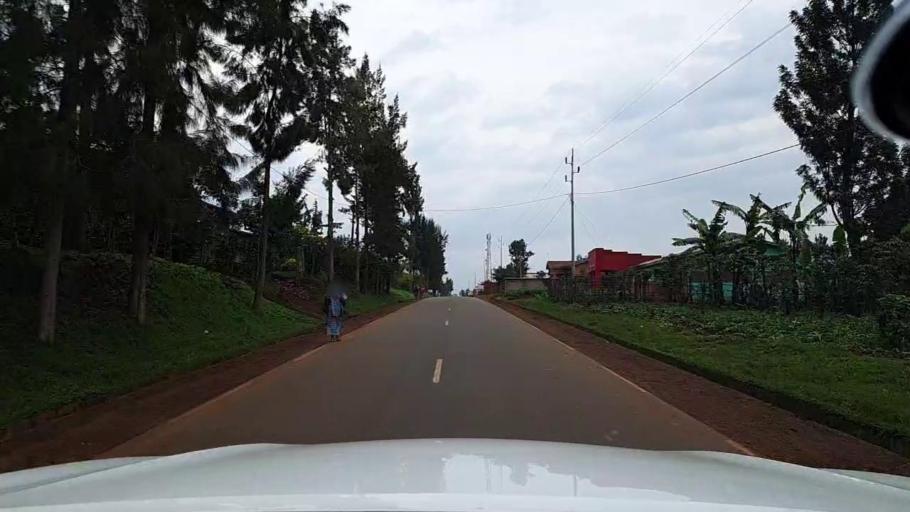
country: RW
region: Western Province
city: Cyangugu
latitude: -2.6240
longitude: 28.9481
